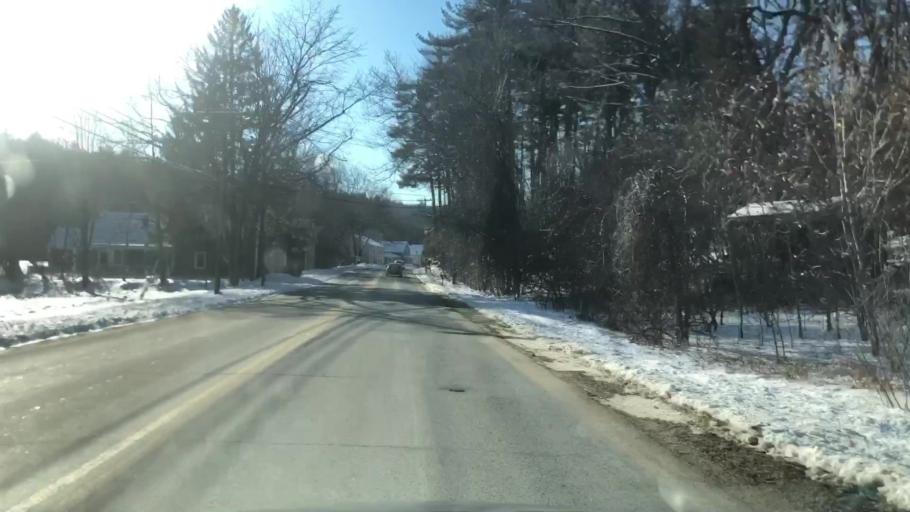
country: US
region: New Hampshire
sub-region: Hillsborough County
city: Wilton
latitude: 42.8404
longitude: -71.7239
